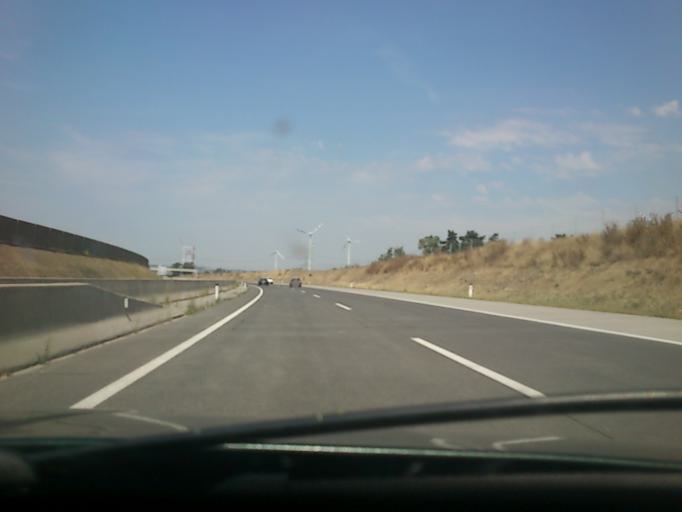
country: AT
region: Lower Austria
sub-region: Politischer Bezirk Mistelbach
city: Pillichsdorf
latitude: 48.3332
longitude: 16.5138
